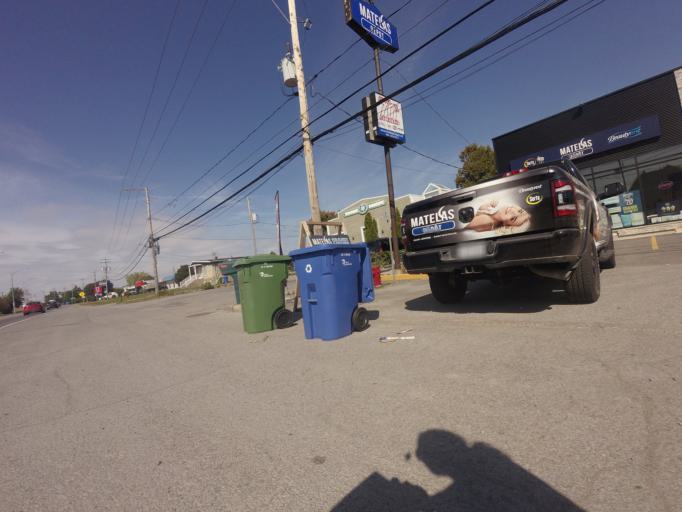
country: CA
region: Quebec
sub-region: Laurentides
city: Saint-Eustache
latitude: 45.5838
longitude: -73.9237
